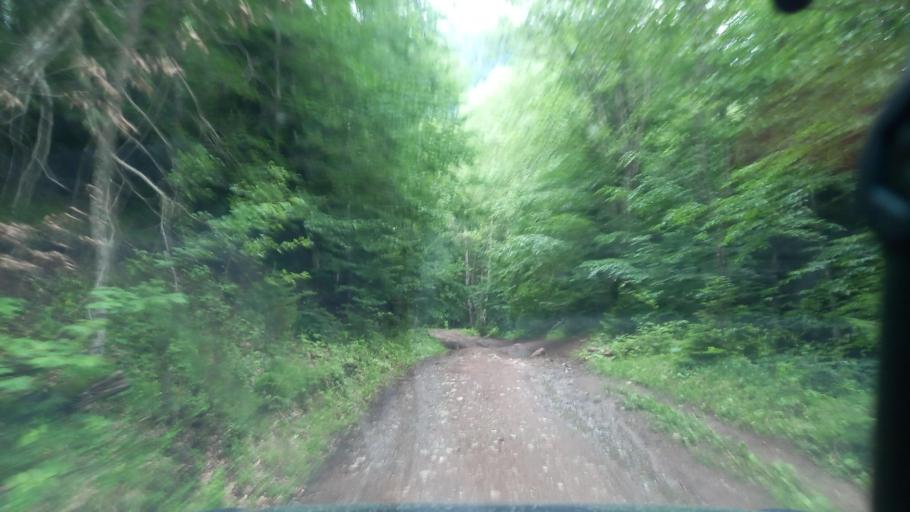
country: RU
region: Karachayevo-Cherkesiya
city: Kurdzhinovo
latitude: 43.8112
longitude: 40.8706
